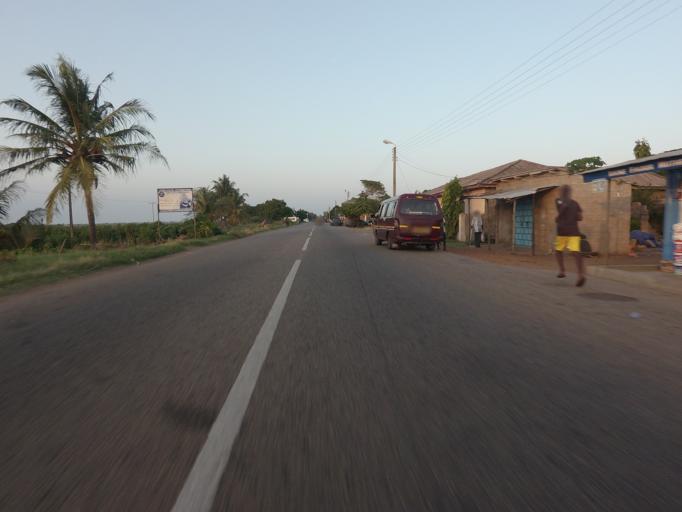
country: GH
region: Volta
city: Anloga
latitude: 5.7981
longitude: 0.9094
